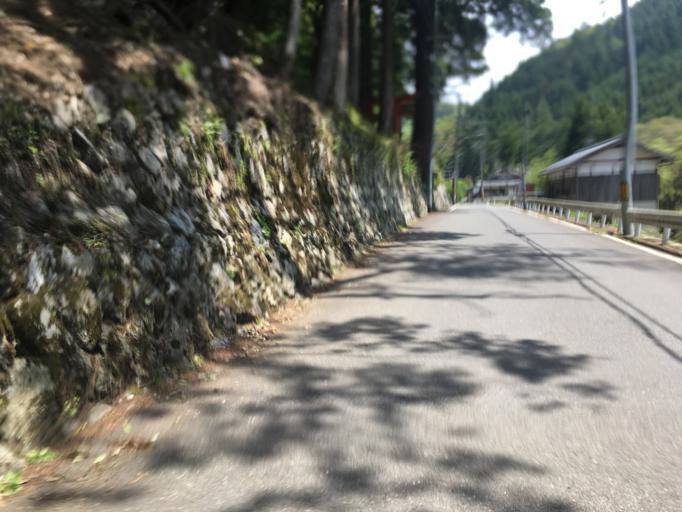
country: JP
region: Kyoto
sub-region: Kyoto-shi
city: Kamigyo-ku
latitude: 35.1139
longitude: 135.7182
